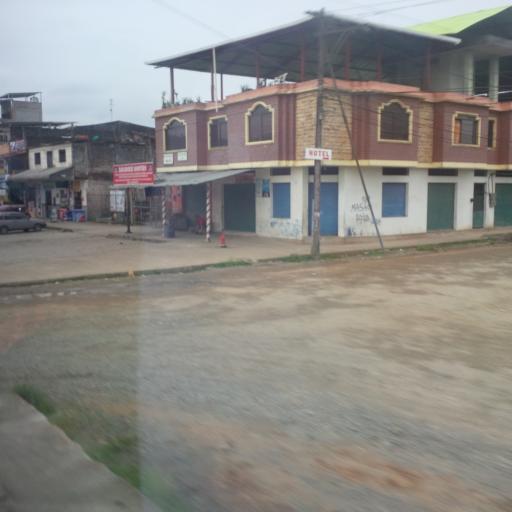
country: EC
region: Chimborazo
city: Alausi
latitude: -2.2083
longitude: -79.1346
